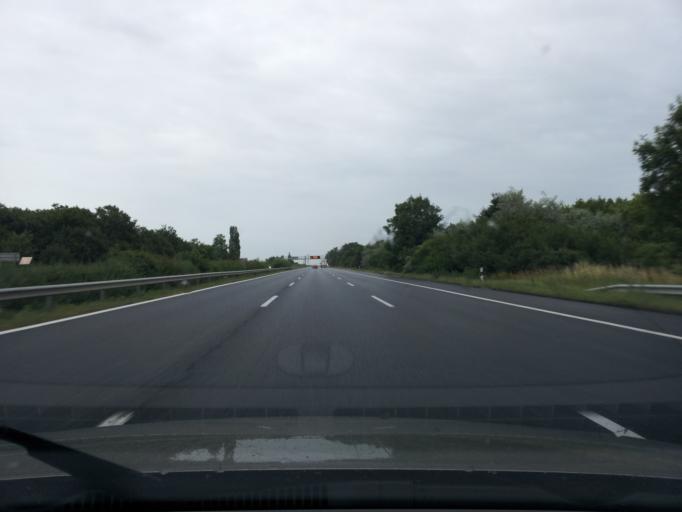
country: HU
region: Fejer
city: Martonvasar
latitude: 47.3408
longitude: 18.7885
